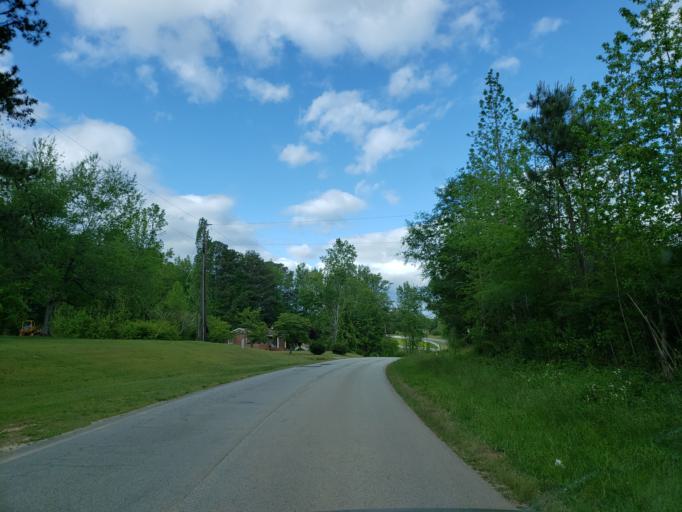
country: US
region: Georgia
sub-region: Haralson County
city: Tallapoosa
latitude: 33.7145
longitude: -85.2971
